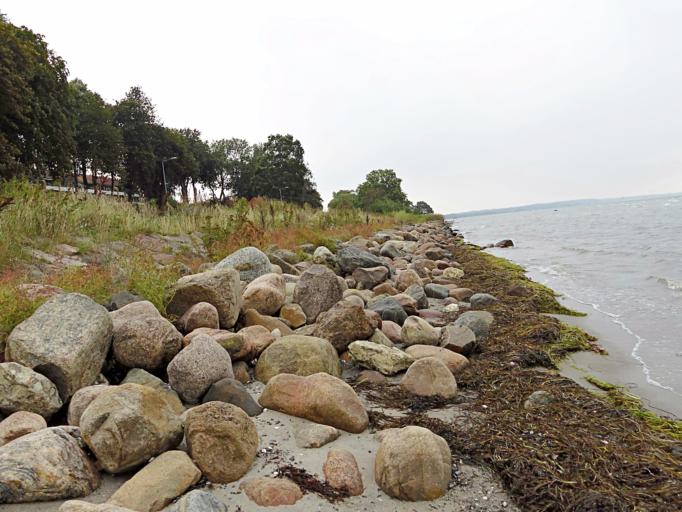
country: DK
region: Capital Region
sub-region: Fredensborg Kommune
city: Kokkedal
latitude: 55.9069
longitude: 12.5276
